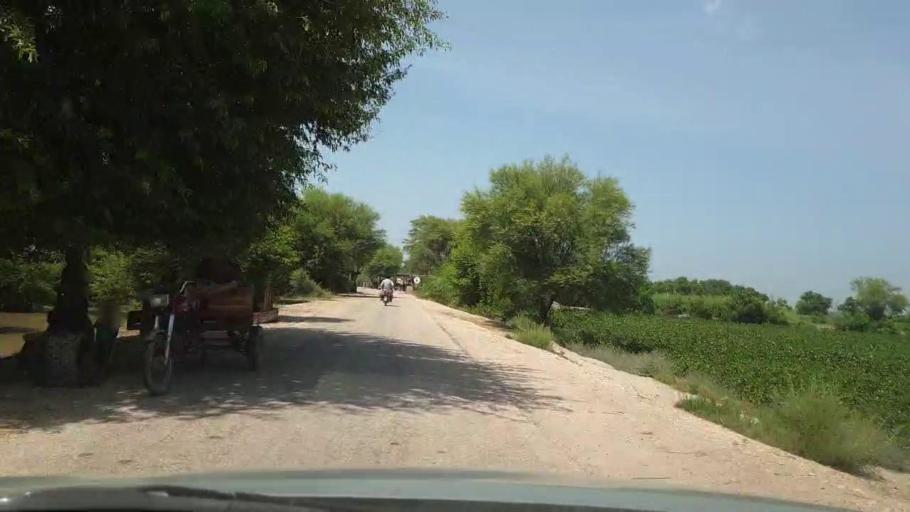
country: PK
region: Sindh
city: Pano Aqil
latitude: 27.7055
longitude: 69.1129
